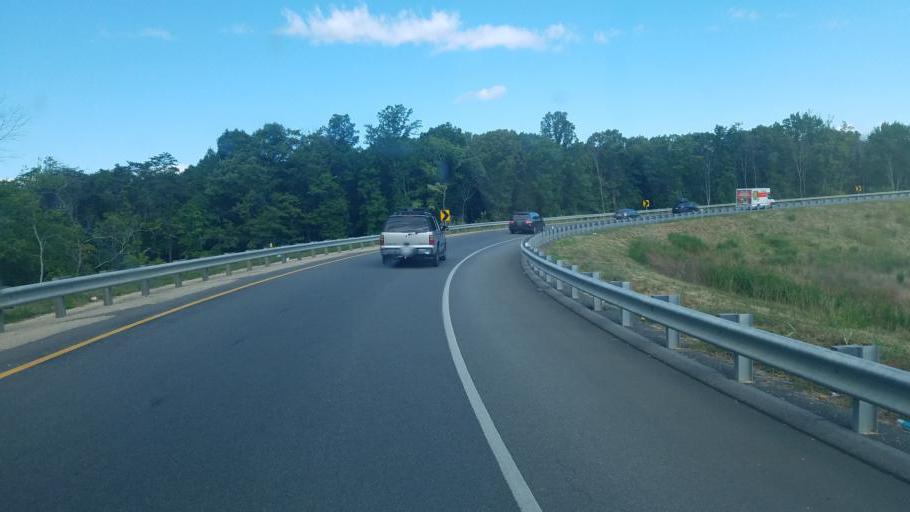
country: US
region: Virginia
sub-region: Fauquier County
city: Bealeton
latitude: 38.6130
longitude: -77.8027
